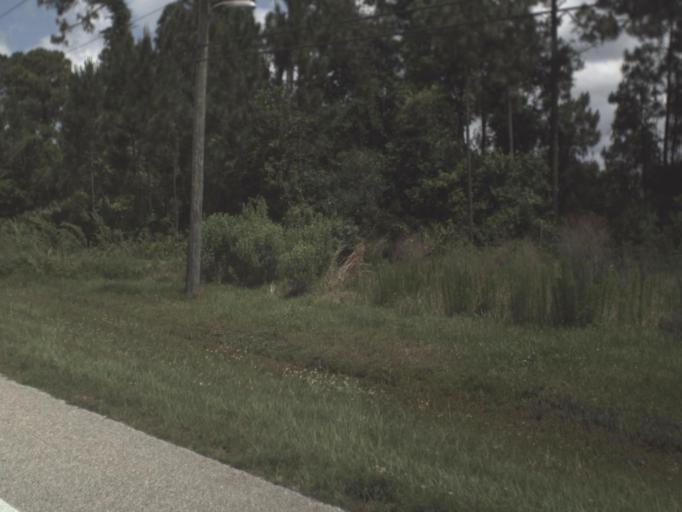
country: US
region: Florida
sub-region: Saint Johns County
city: Palm Valley
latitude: 30.0728
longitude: -81.4465
